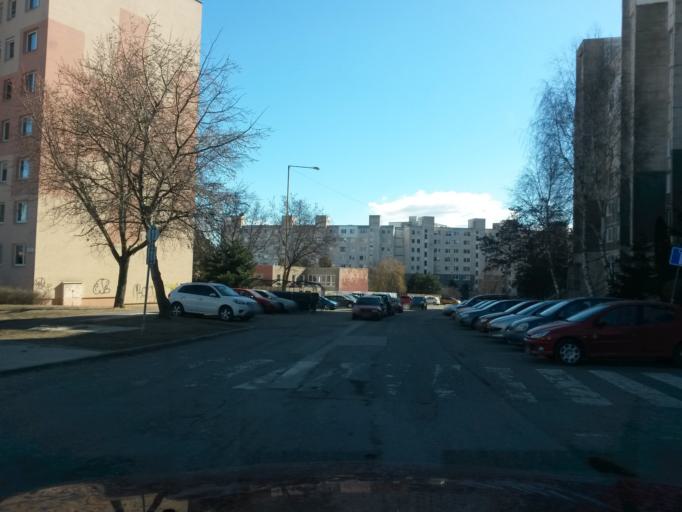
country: SK
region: Kosicky
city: Kosice
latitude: 48.7188
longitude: 21.2101
